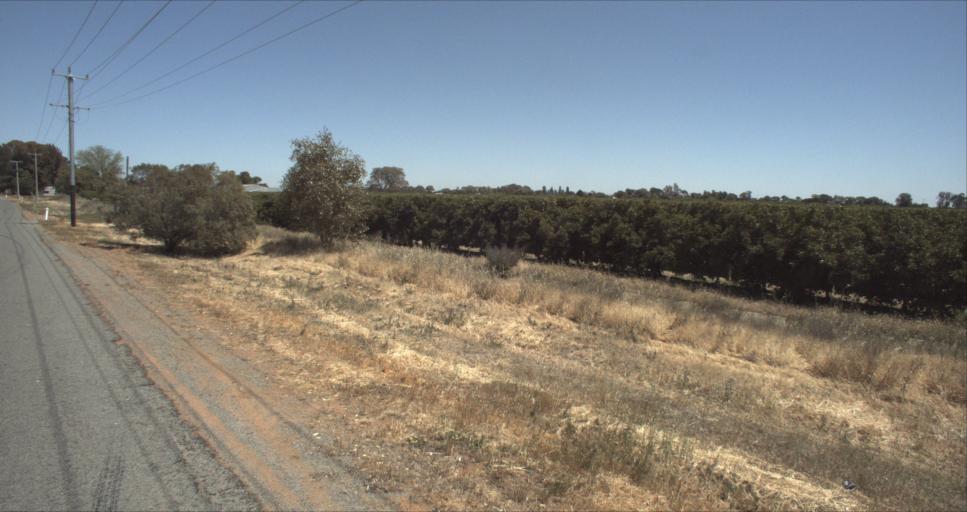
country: AU
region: New South Wales
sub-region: Leeton
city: Leeton
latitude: -34.5360
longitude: 146.3970
